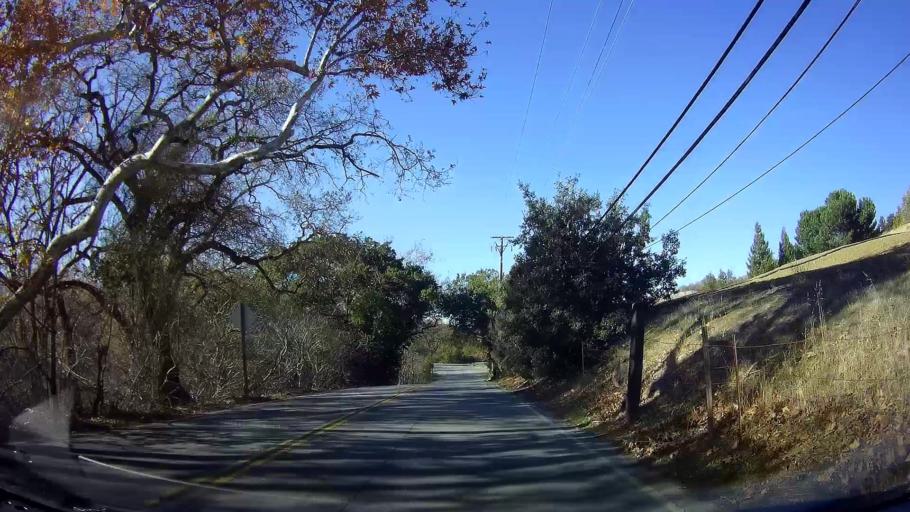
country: US
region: California
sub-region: Santa Clara County
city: Seven Trees
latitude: 37.2223
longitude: -121.8494
